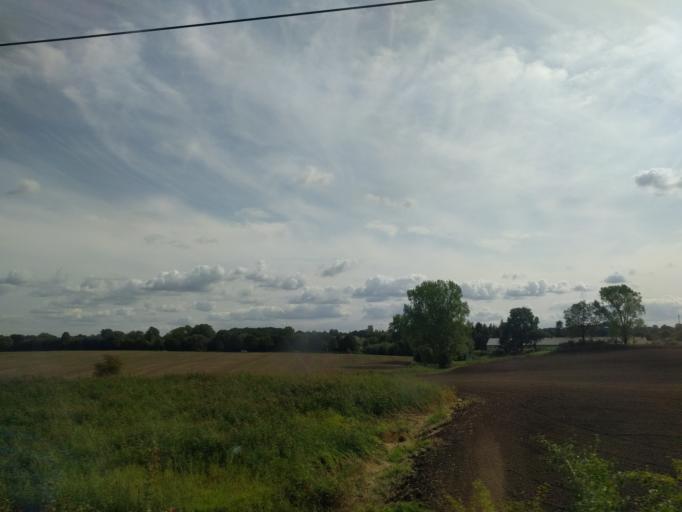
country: DE
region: Schleswig-Holstein
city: Meddewade
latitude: 53.8234
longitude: 10.4566
